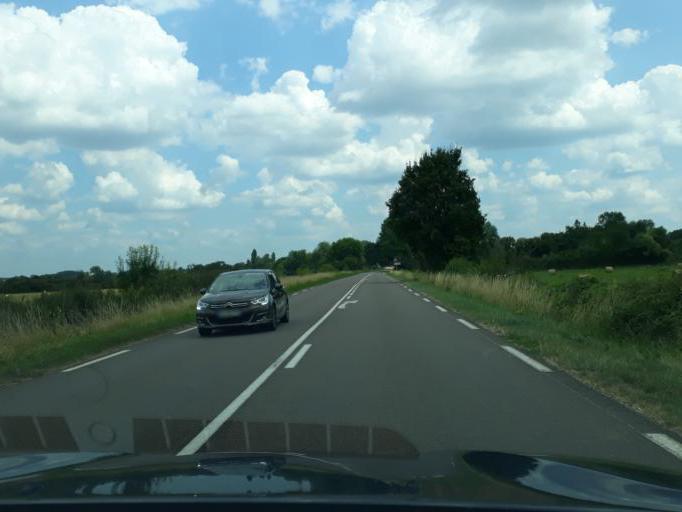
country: FR
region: Centre
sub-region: Departement du Cher
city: Nerondes
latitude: 46.9988
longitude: 2.7904
